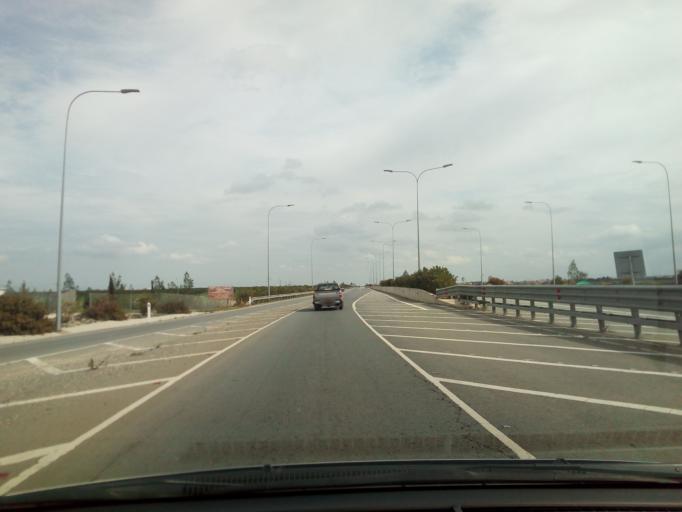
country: CY
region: Lefkosia
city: Kokkinotrimithia
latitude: 35.1618
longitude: 33.1643
